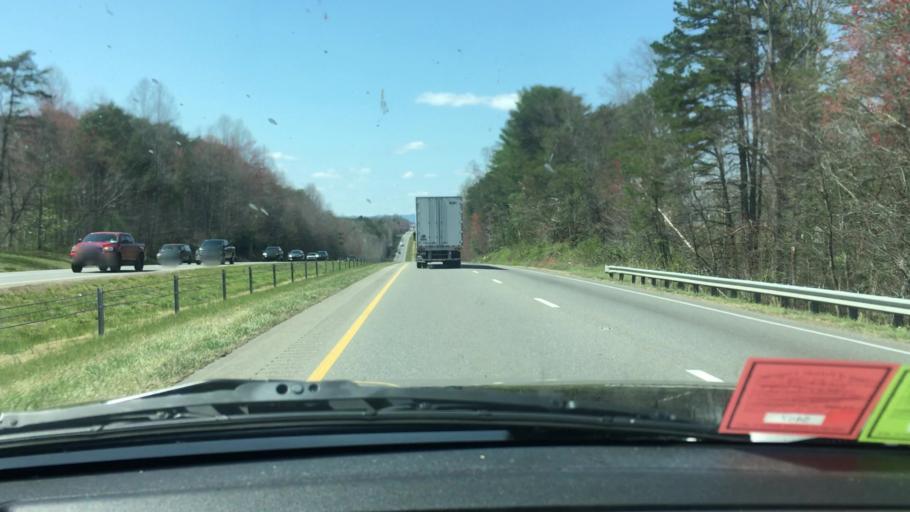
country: US
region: North Carolina
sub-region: Surry County
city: Pilot Mountain
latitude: 36.4214
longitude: -80.5150
